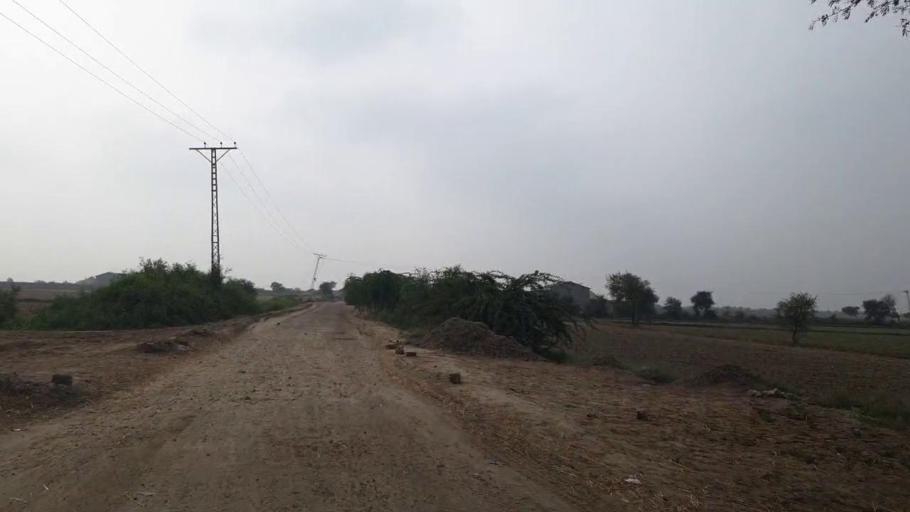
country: PK
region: Sindh
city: Matli
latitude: 24.9415
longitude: 68.5749
